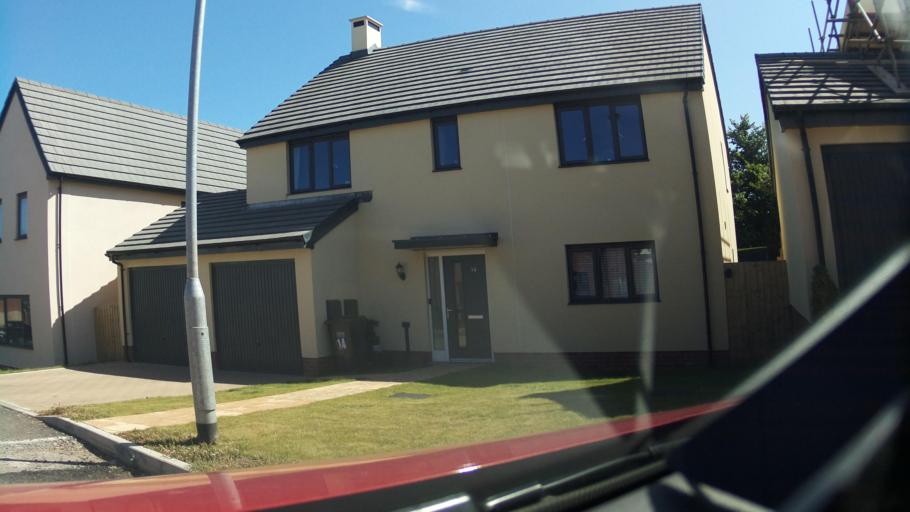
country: GB
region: England
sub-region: Borough of Torbay
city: Paignton
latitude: 50.4106
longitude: -3.5834
